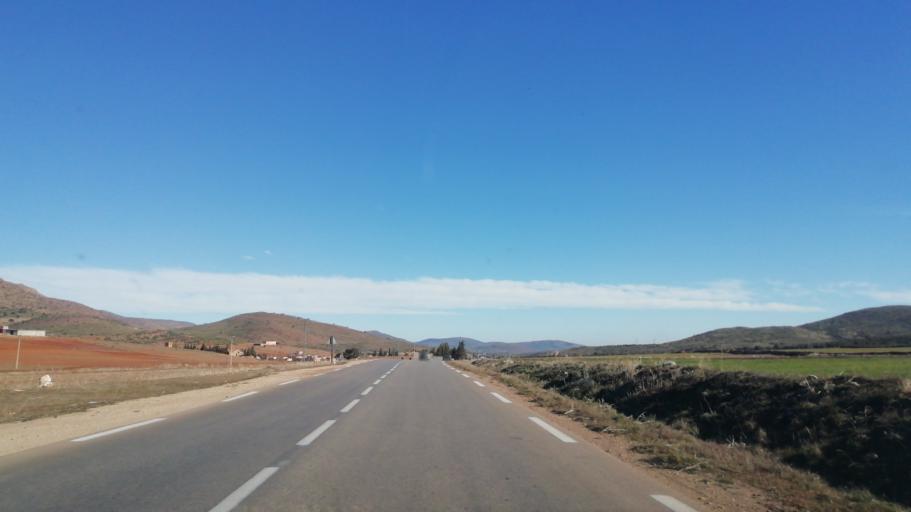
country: DZ
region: Tlemcen
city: Sebdou
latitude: 34.7385
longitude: -1.1713
